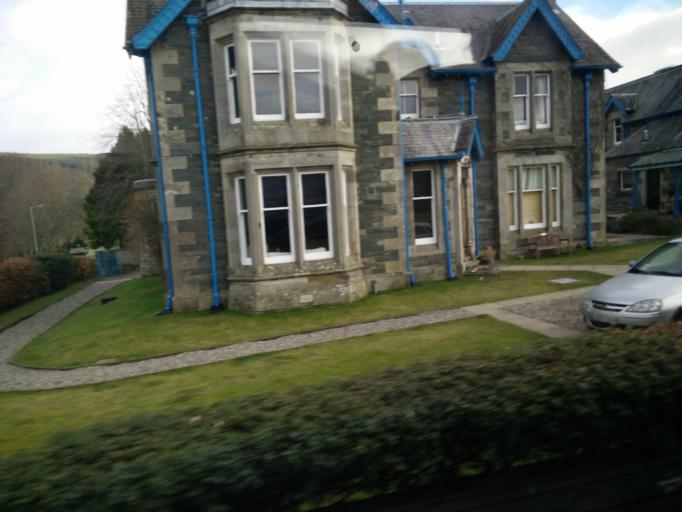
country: GB
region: Scotland
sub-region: Perth and Kinross
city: Aberfeldy
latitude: 56.6212
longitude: -3.8721
